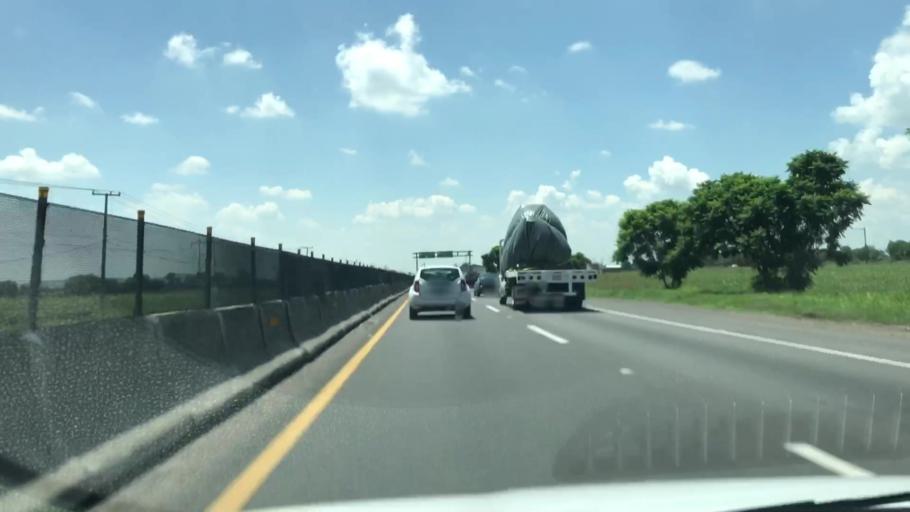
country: MX
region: Guanajuato
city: Sarabia
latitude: 20.5182
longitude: -101.0459
